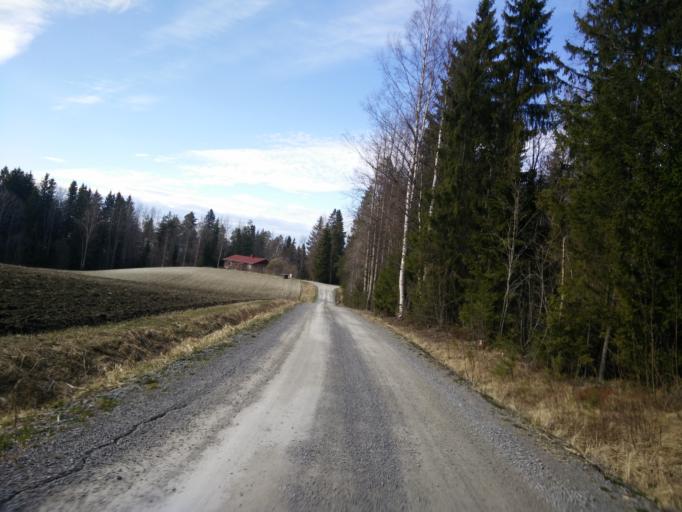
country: FI
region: Pirkanmaa
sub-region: Tampere
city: Orivesi
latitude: 61.6979
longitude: 24.3658
